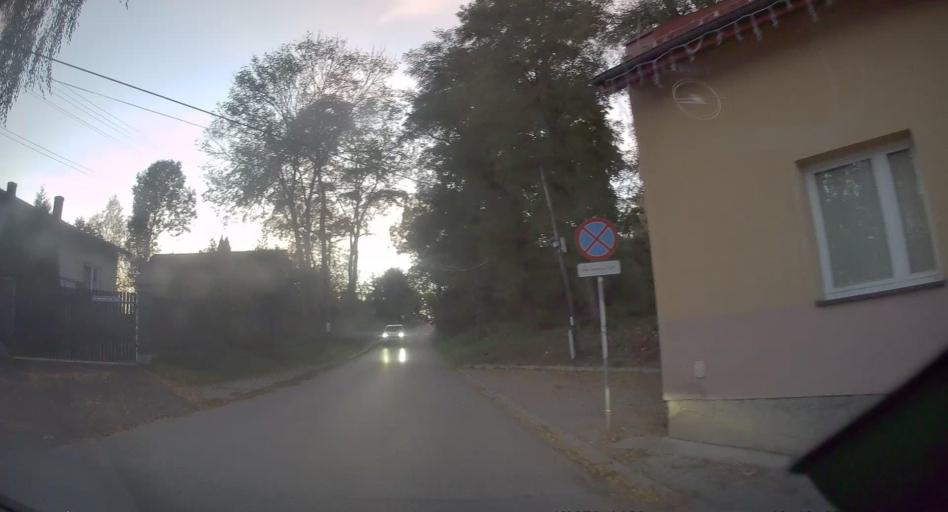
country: PL
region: Lesser Poland Voivodeship
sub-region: Powiat krakowski
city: Bolechowice
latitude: 50.1372
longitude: 19.8183
